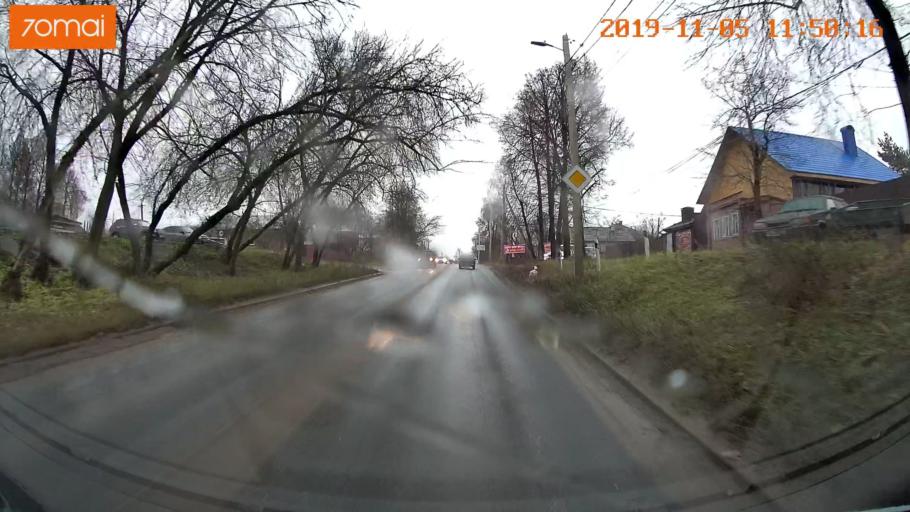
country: RU
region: Ivanovo
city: Bogorodskoye
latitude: 57.0068
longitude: 41.0134
